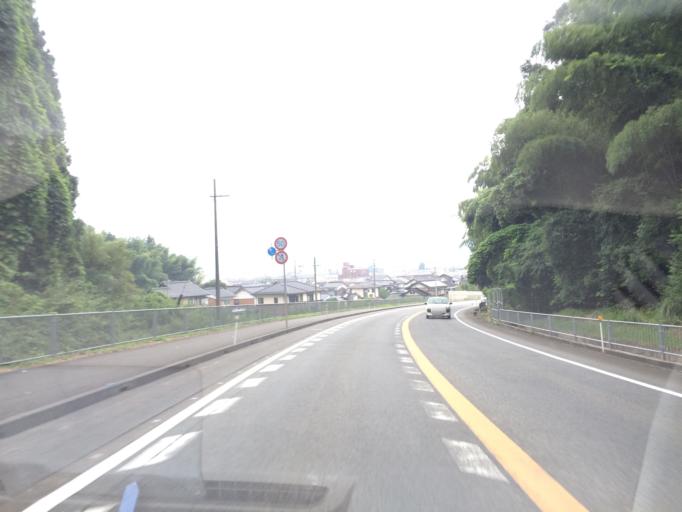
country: JP
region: Hyogo
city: Toyooka
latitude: 35.5274
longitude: 134.8144
